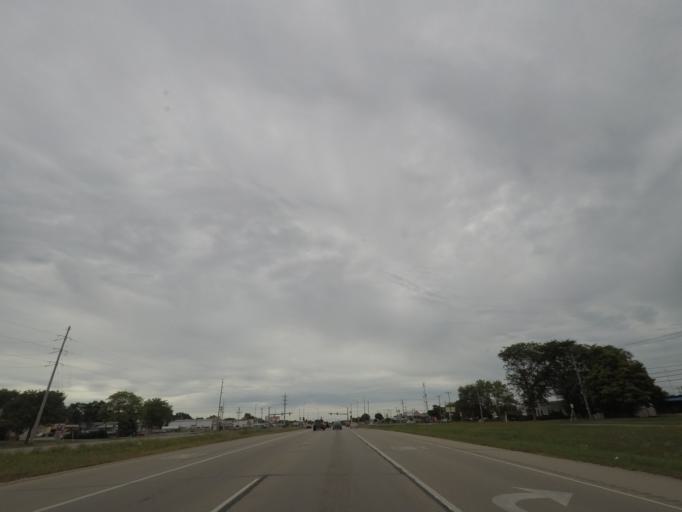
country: US
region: Wisconsin
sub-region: Dane County
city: Monona
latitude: 43.0605
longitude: -89.3093
